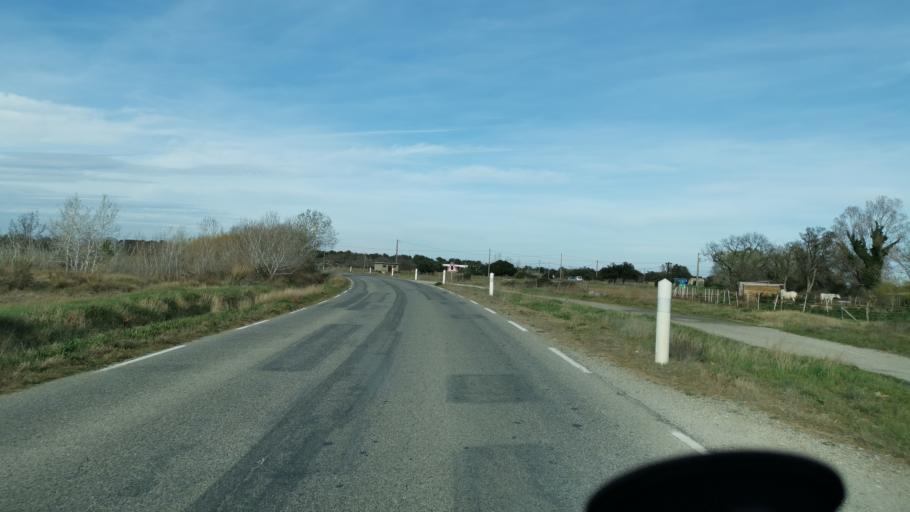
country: FR
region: Provence-Alpes-Cote d'Azur
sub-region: Departement des Bouches-du-Rhone
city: Saint-Martin-de-Crau
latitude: 43.5635
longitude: 4.7390
